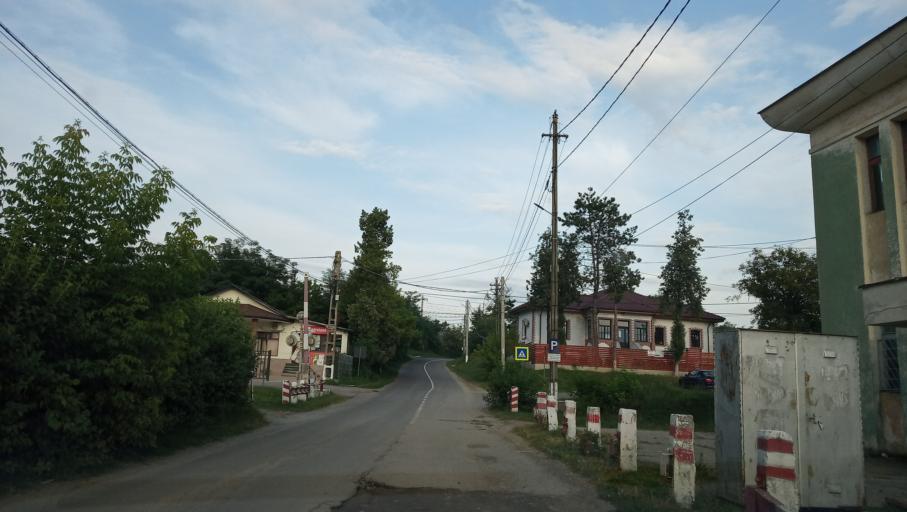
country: RO
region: Giurgiu
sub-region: Comuna Comana
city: Comana
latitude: 44.1725
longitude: 26.1470
